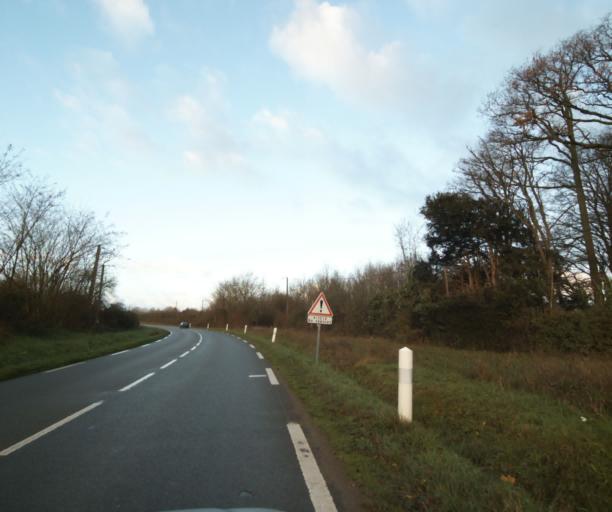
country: FR
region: Pays de la Loire
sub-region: Departement de la Sarthe
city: Sarge-les-le-Mans
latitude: 48.0176
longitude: 0.2572
